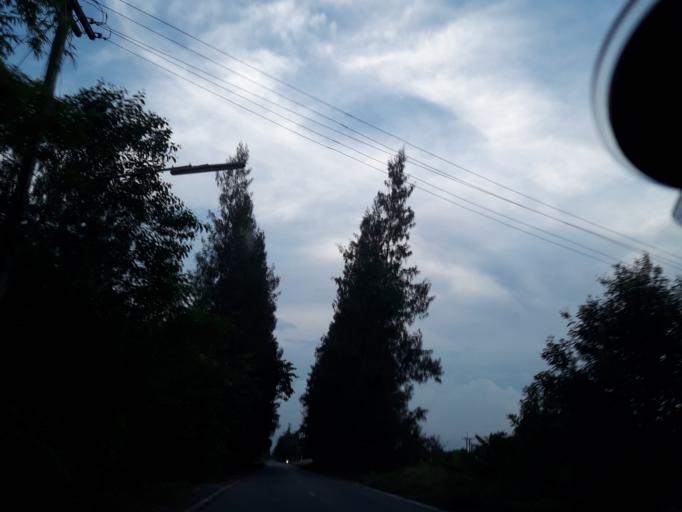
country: TH
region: Pathum Thani
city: Nong Suea
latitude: 14.1710
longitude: 100.8689
